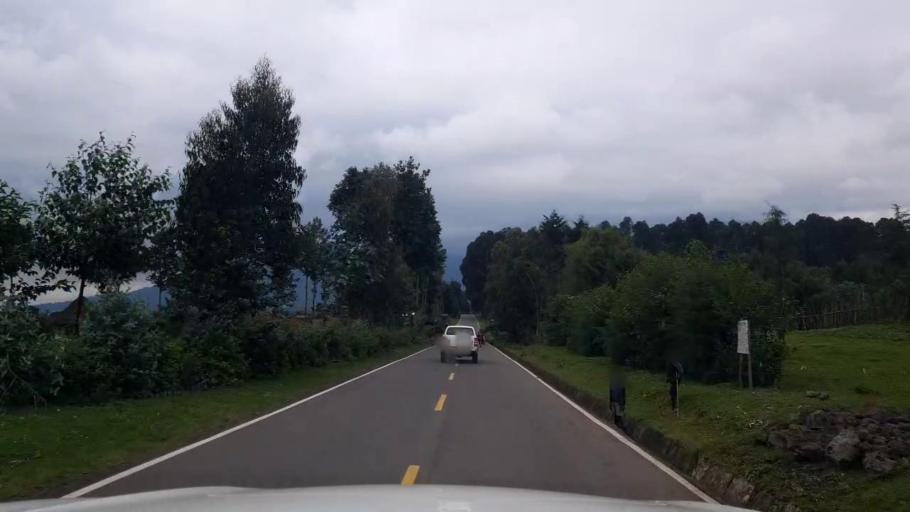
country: RW
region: Northern Province
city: Musanze
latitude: -1.4311
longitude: 29.5604
